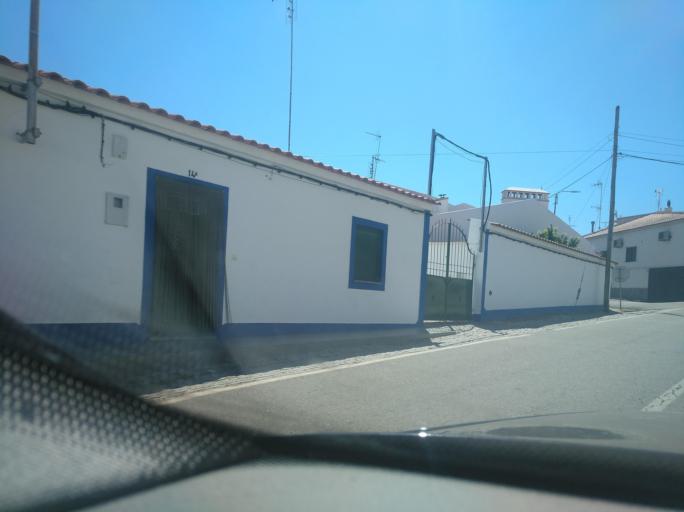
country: PT
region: Portalegre
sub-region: Elvas
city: Elvas
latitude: 38.9617
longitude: -7.2986
